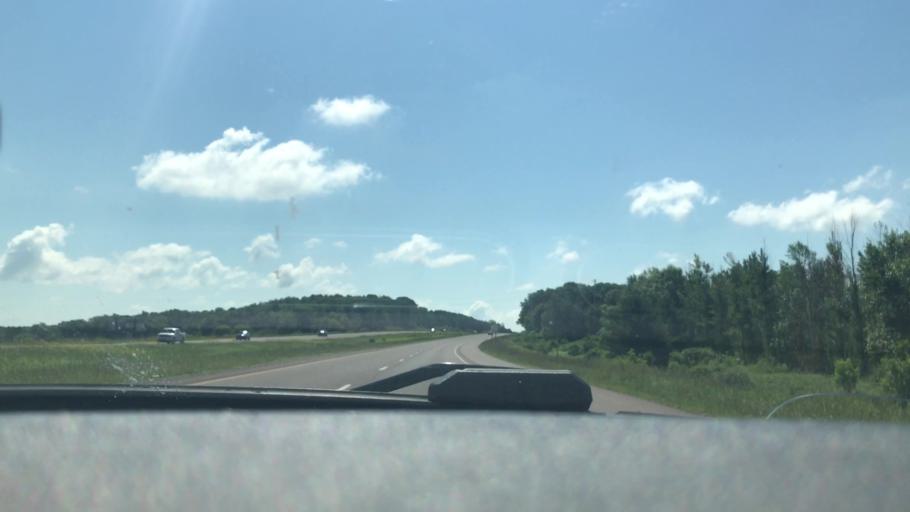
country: US
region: Wisconsin
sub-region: Chippewa County
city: Bloomer
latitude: 45.0909
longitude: -91.4916
